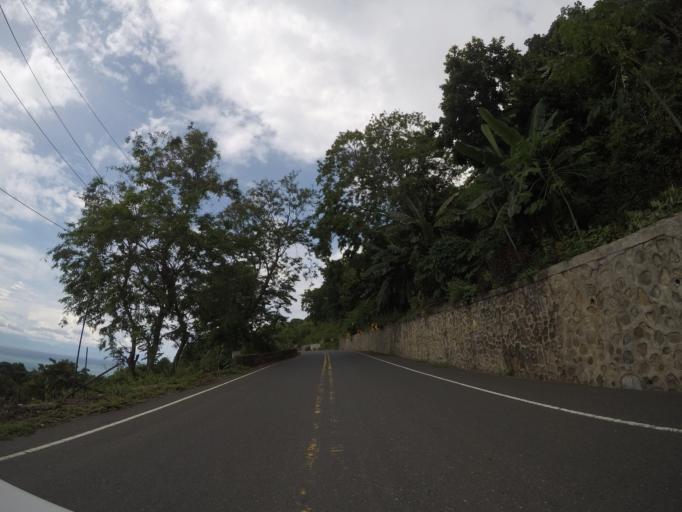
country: TL
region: Liquica
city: Maubara
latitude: -8.6640
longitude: 125.1136
